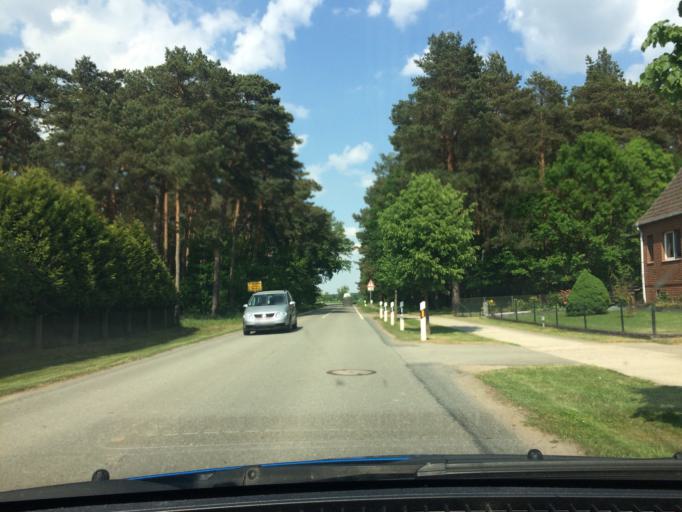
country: DE
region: Lower Saxony
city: Neu Darchau
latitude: 53.2645
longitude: 10.9203
